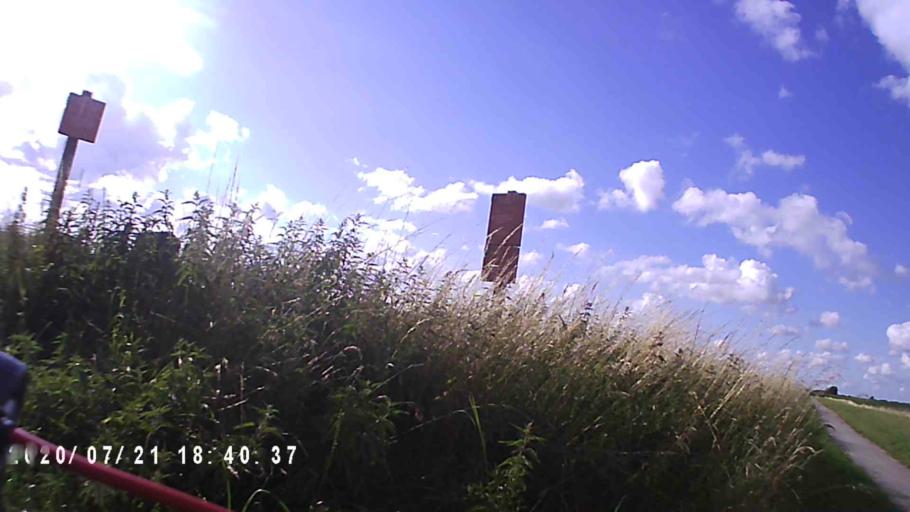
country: NL
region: Groningen
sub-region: Gemeente Hoogezand-Sappemeer
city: Hoogezand
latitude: 53.1987
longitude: 6.7484
